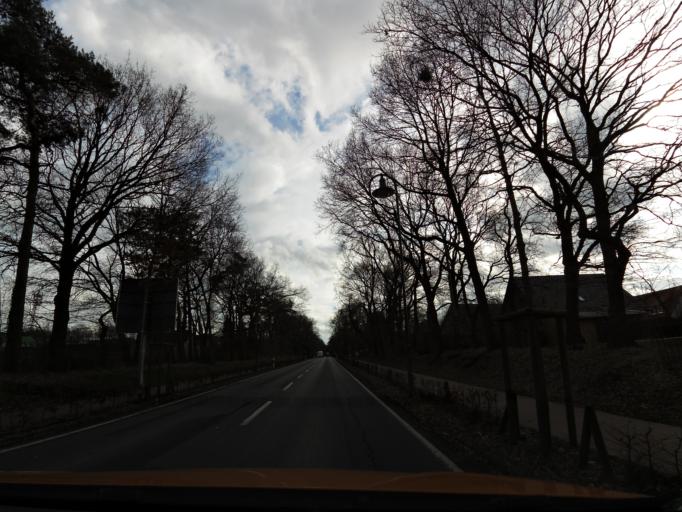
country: DE
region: Lower Saxony
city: Dotlingen
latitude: 52.9726
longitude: 8.3981
